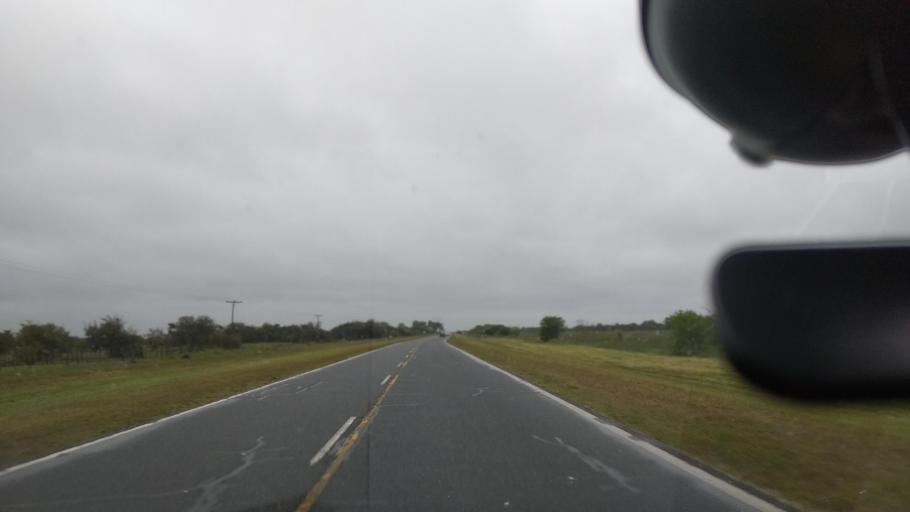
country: AR
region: Buenos Aires
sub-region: Partido de Castelli
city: Castelli
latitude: -35.9074
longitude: -57.4407
